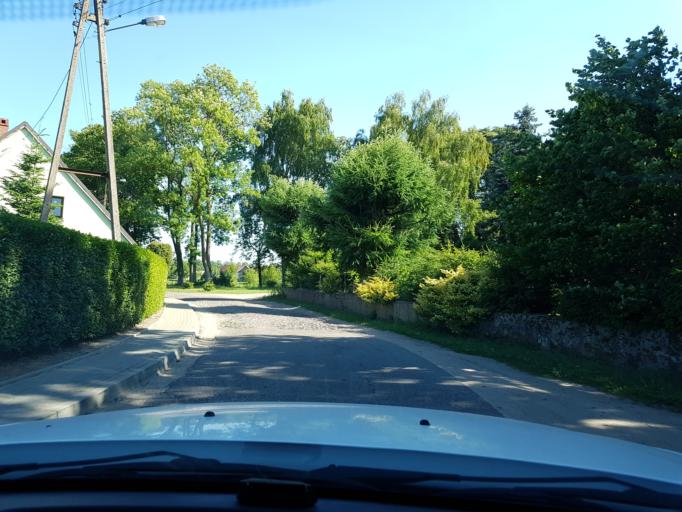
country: PL
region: West Pomeranian Voivodeship
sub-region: Powiat swidwinski
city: Slawoborze
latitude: 53.8447
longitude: 15.7077
